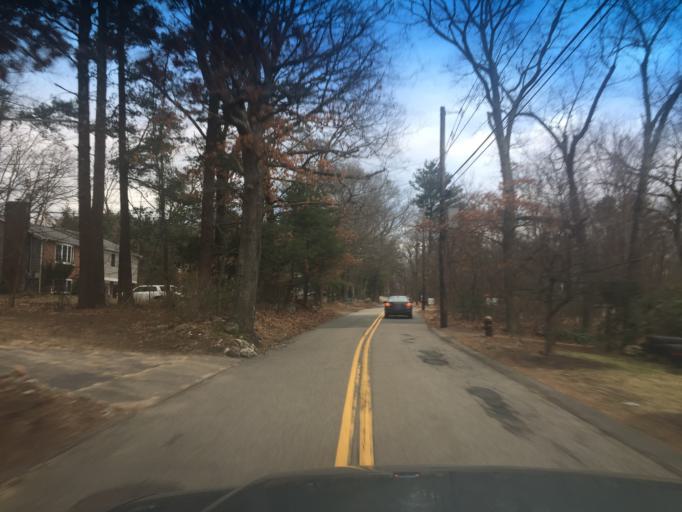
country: US
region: Massachusetts
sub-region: Norfolk County
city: Medway
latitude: 42.1456
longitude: -71.3809
